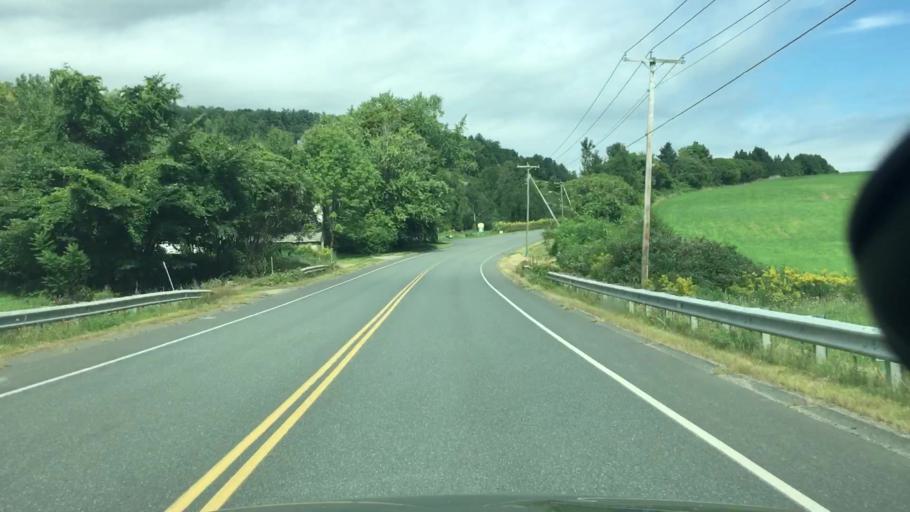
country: US
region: Massachusetts
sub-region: Franklin County
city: Colrain
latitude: 42.6420
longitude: -72.6735
